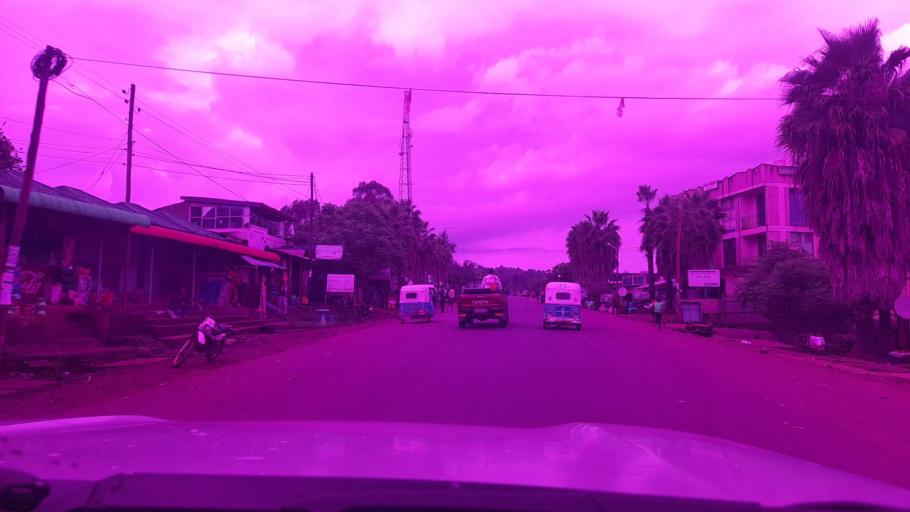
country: ET
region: Oromiya
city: Jima
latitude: 7.9256
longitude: 37.4177
